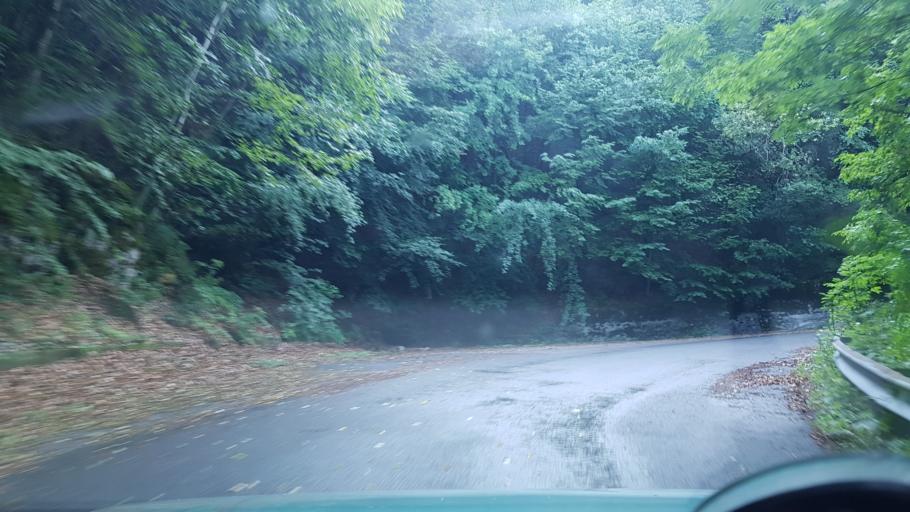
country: IT
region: Friuli Venezia Giulia
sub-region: Provincia di Udine
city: Lusevera
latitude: 46.3095
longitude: 13.2587
